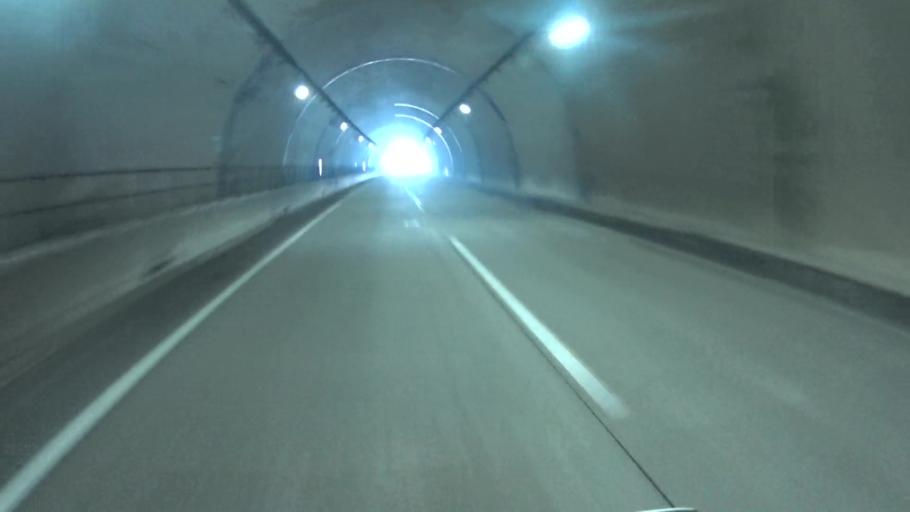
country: JP
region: Kyoto
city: Kameoka
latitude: 35.0689
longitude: 135.5209
